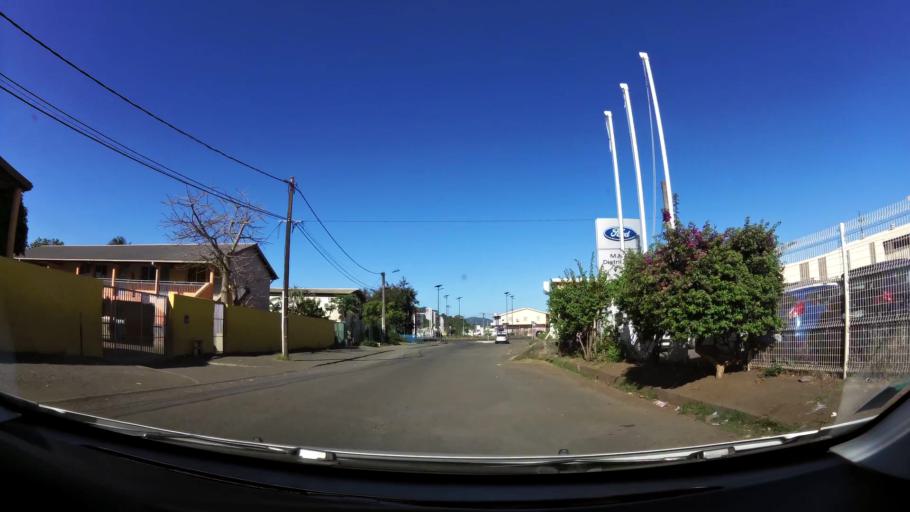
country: YT
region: Mamoudzou
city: Mamoudzou
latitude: -12.7710
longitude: 45.2227
